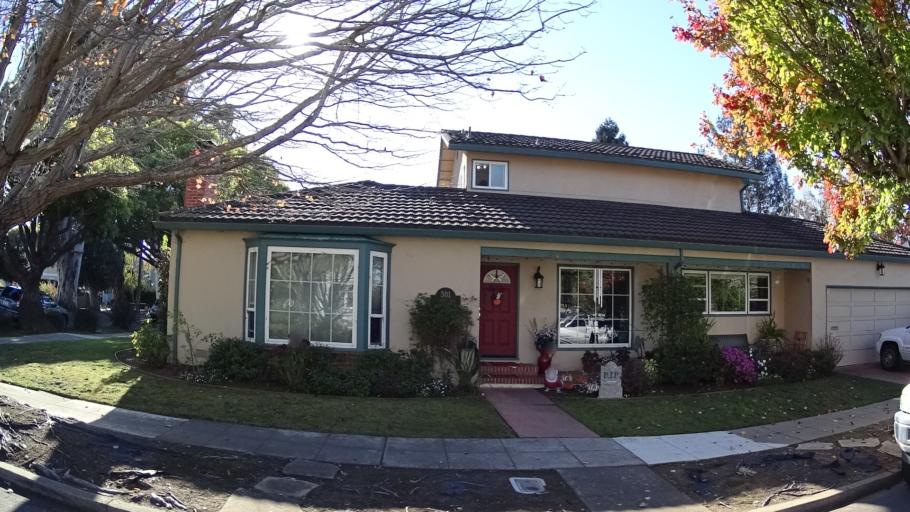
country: US
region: California
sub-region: San Mateo County
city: San Mateo
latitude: 37.5855
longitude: -122.3376
